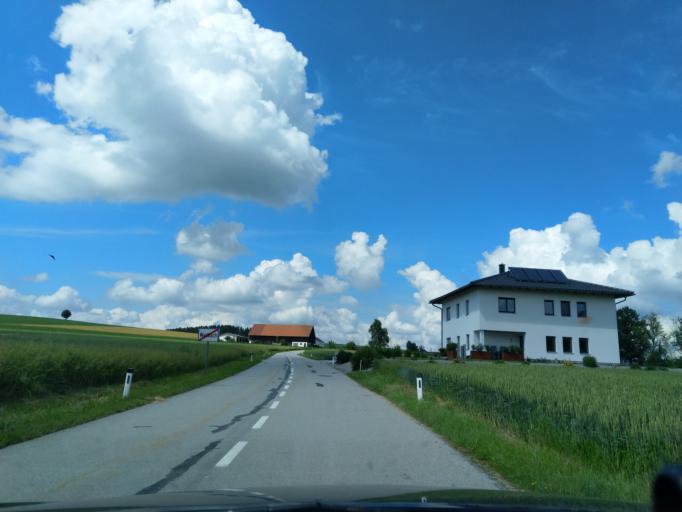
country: DE
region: Bavaria
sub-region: Lower Bavaria
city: Bad Fussing
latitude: 48.2804
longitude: 13.3690
